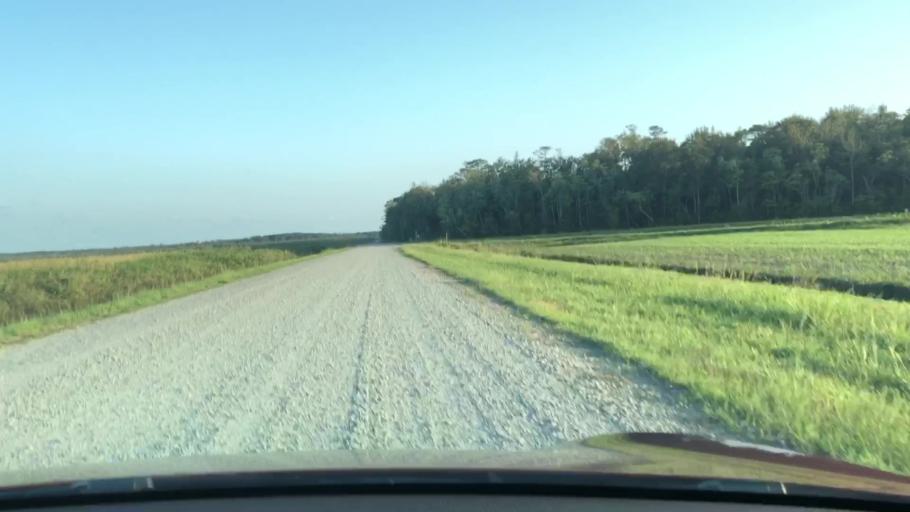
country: US
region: North Carolina
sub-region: Dare County
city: Manteo
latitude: 35.8460
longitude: -75.8607
